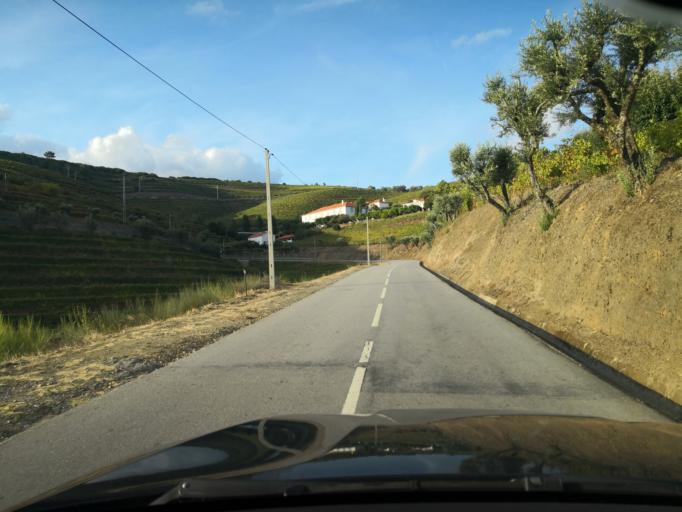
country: PT
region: Vila Real
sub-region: Santa Marta de Penaguiao
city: Santa Marta de Penaguiao
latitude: 41.2081
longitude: -7.8042
